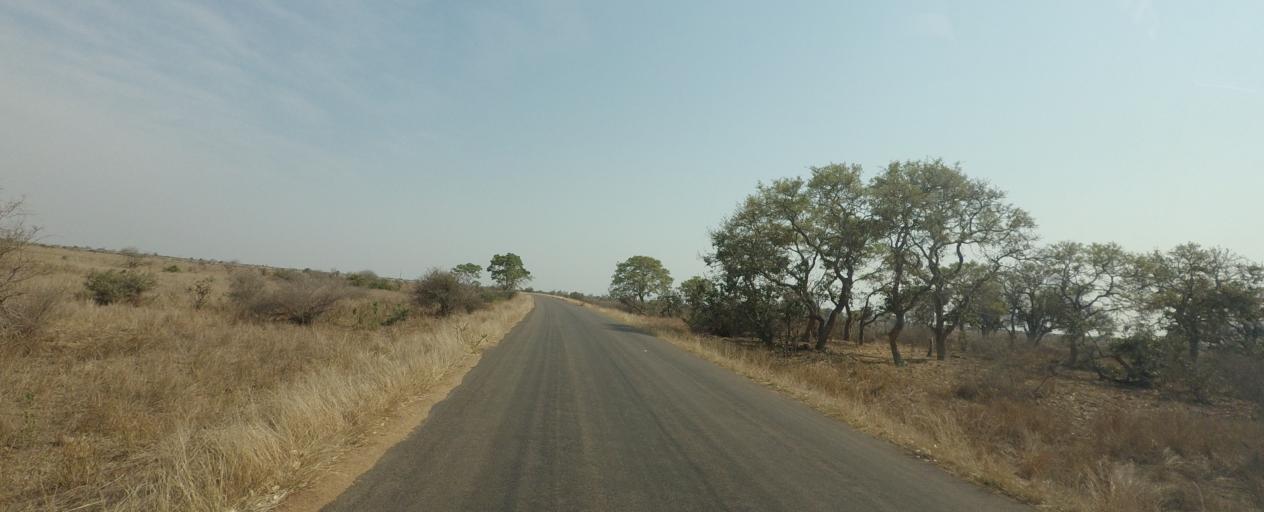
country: ZA
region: Limpopo
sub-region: Mopani District Municipality
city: Phalaborwa
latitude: -24.2813
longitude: 31.7405
